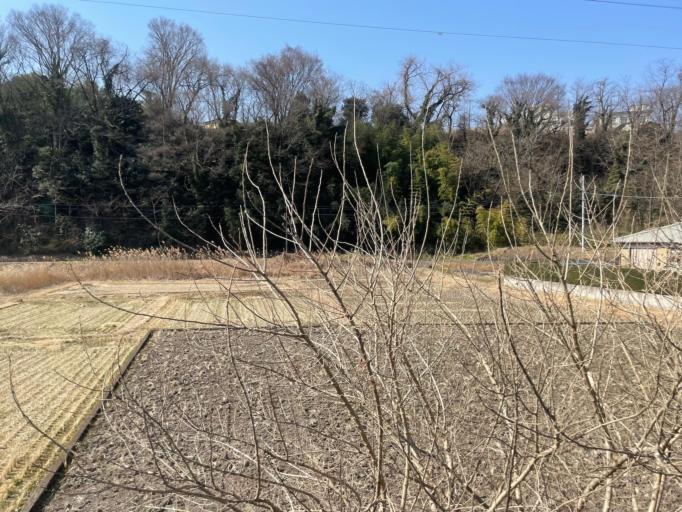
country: JP
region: Gunma
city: Shibukawa
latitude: 36.5218
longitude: 138.9904
